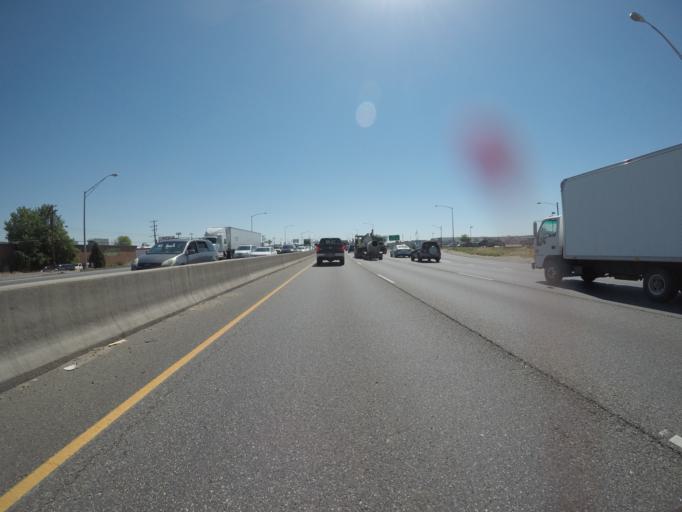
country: US
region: Colorado
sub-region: Adams County
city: Commerce City
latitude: 39.7801
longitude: -104.9365
